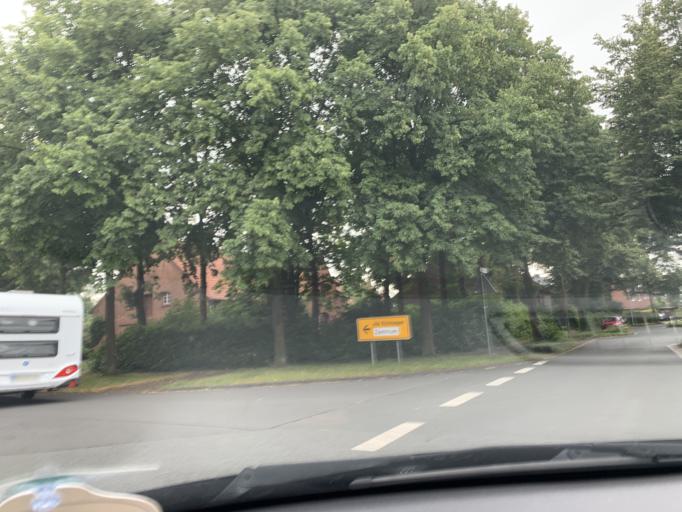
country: DE
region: North Rhine-Westphalia
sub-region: Regierungsbezirk Munster
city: Ostbevern
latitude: 52.0422
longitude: 7.8388
